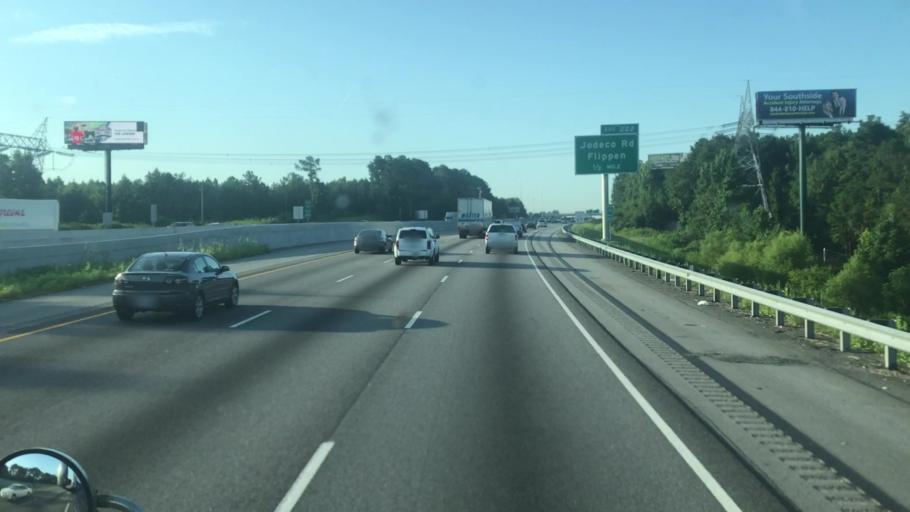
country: US
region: Georgia
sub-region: Henry County
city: Stockbridge
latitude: 33.4935
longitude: -84.2208
